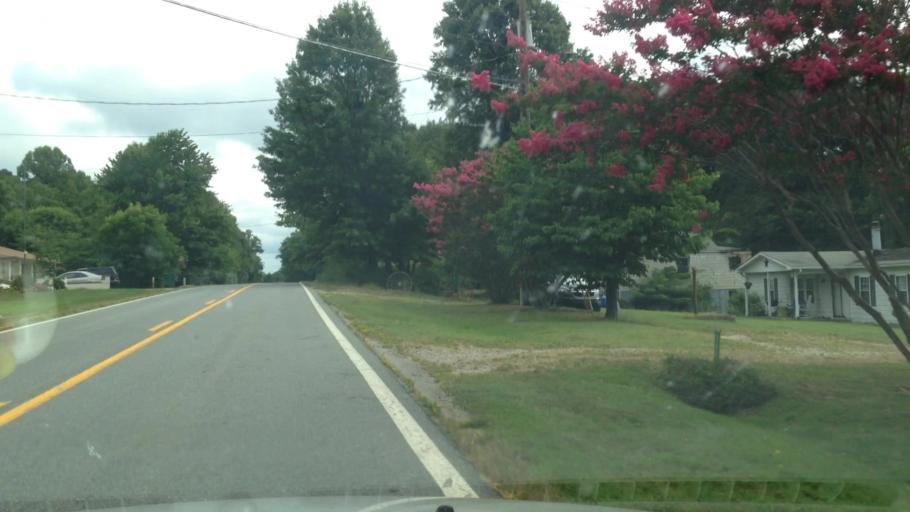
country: US
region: North Carolina
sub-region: Rockingham County
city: Reidsville
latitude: 36.4209
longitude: -79.5912
